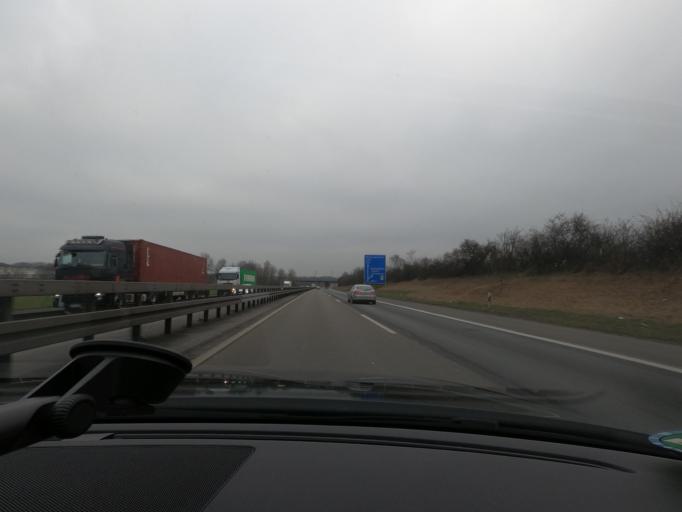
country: DE
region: North Rhine-Westphalia
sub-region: Regierungsbezirk Dusseldorf
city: Monchengladbach
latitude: 51.1463
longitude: 6.4141
